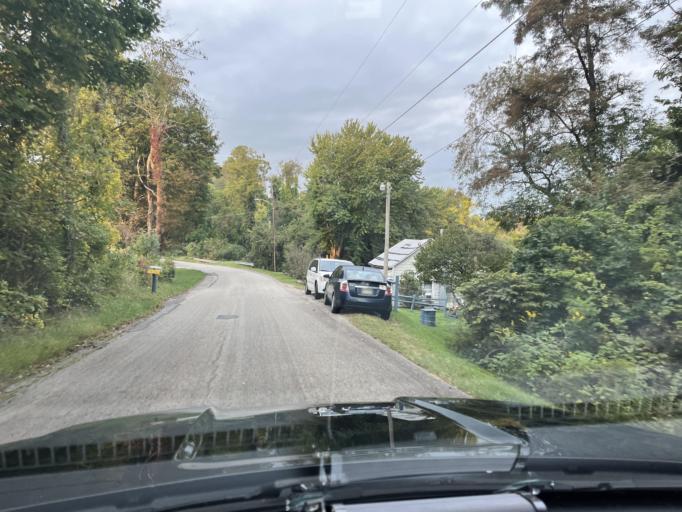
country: US
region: Pennsylvania
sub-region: Fayette County
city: South Uniontown
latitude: 39.8884
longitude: -79.7712
